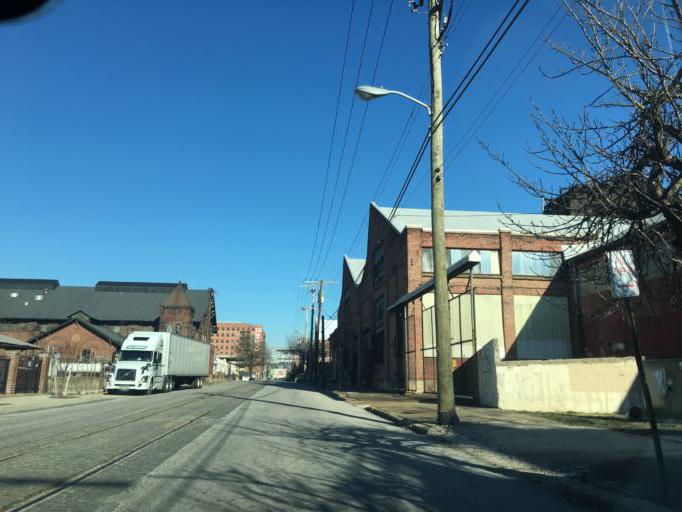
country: US
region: Maryland
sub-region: City of Baltimore
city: Baltimore
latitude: 39.2768
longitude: -76.6324
